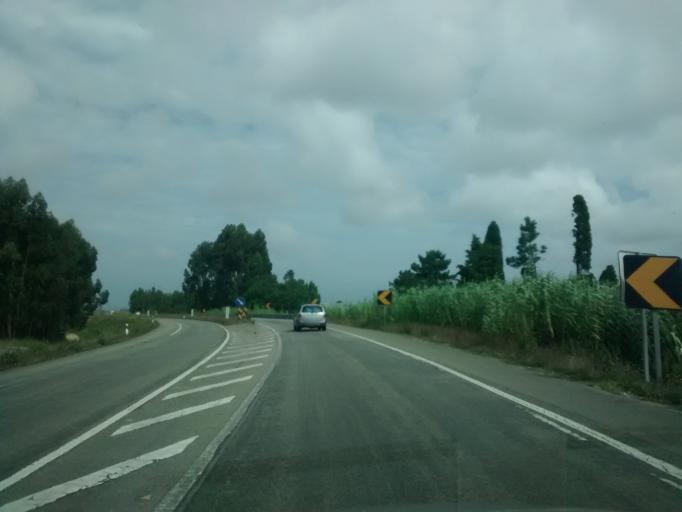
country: PT
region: Aveiro
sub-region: Aveiro
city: Oliveirinha
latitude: 40.5965
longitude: -8.6127
